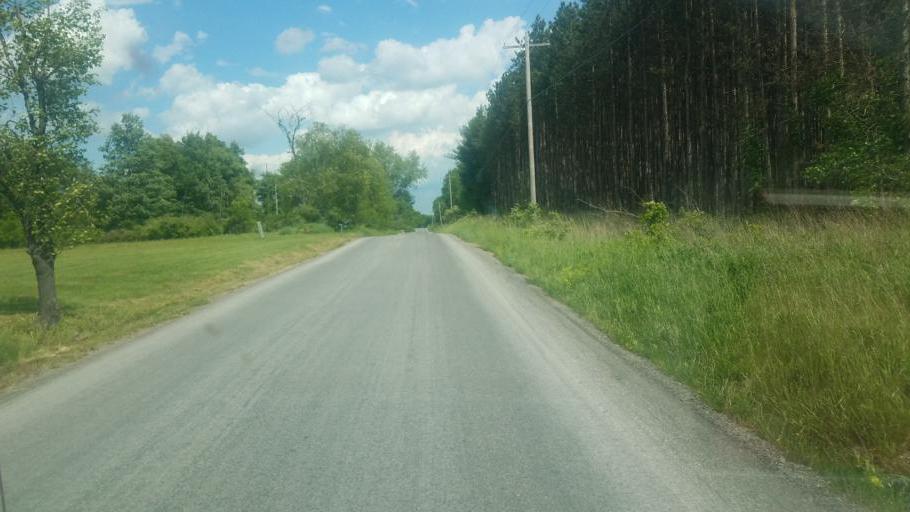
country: US
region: Pennsylvania
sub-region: Venango County
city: Franklin
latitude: 41.2265
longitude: -79.8346
